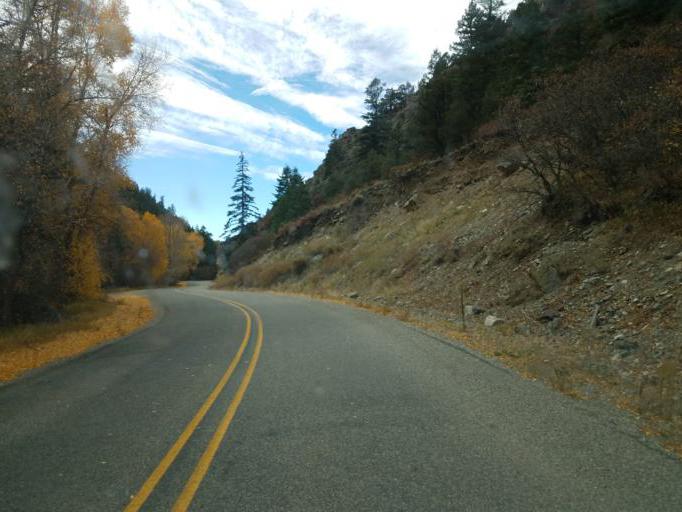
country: US
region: New Mexico
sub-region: Taos County
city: Arroyo Seco
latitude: 36.5436
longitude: -105.5552
